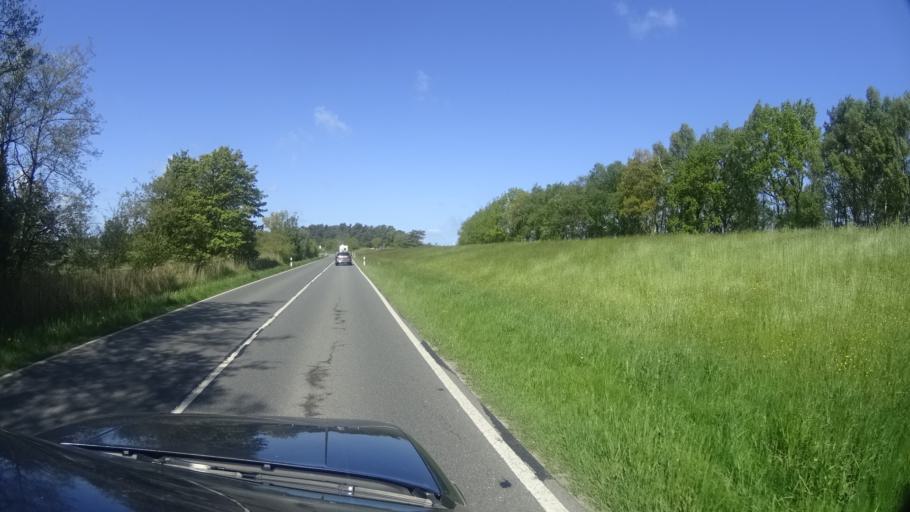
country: DE
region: Mecklenburg-Vorpommern
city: Ostseebad Prerow
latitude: 54.4498
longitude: 12.5980
